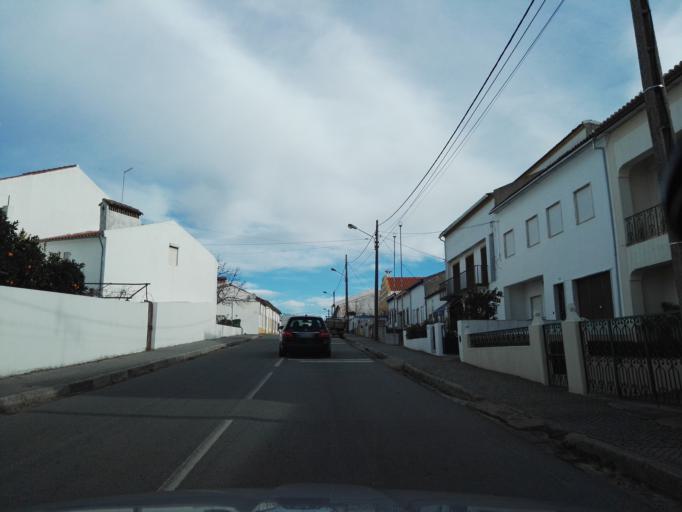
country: PT
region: Portalegre
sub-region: Nisa
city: Nisa
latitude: 39.5137
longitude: -7.6544
